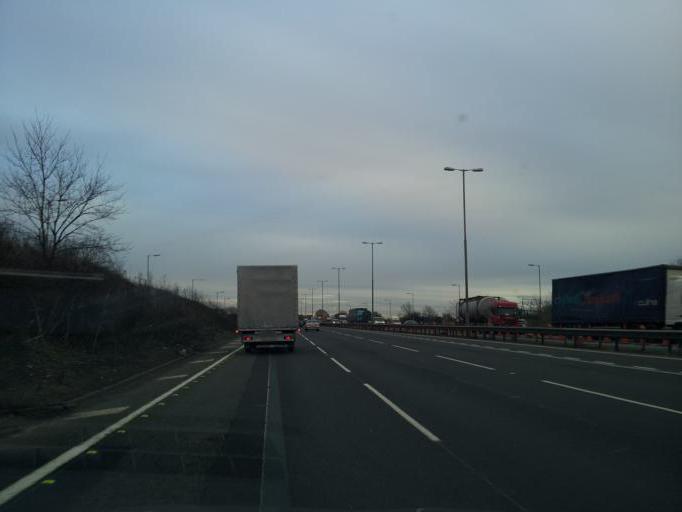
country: GB
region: England
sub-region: Northamptonshire
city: Bugbrooke
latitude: 52.2300
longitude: -1.0142
